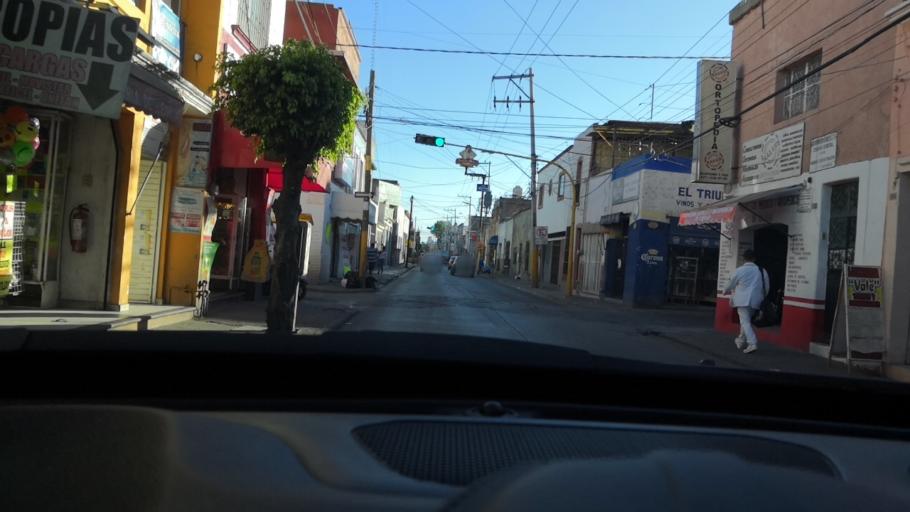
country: MX
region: Guanajuato
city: Leon
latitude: 21.1319
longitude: -101.6801
